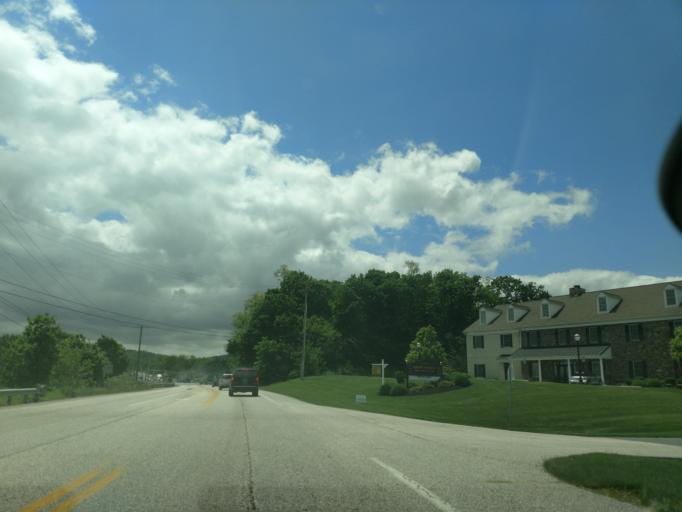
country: US
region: Pennsylvania
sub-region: Lebanon County
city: Cornwall
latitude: 40.2813
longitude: -76.4339
